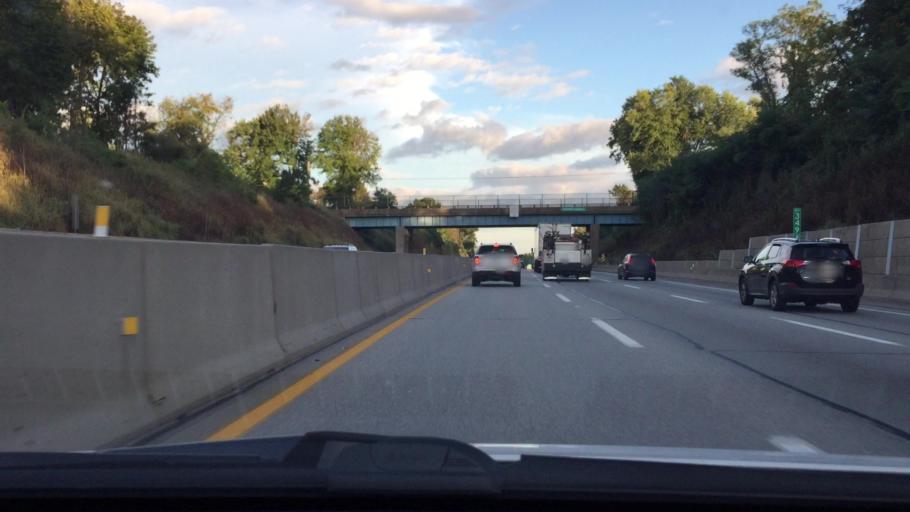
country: US
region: Pennsylvania
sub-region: Bucks County
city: Feasterville
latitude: 40.1433
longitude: -75.0038
